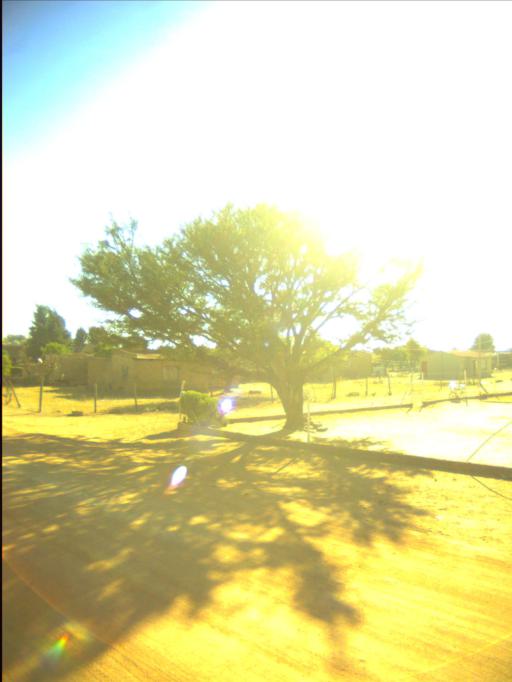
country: ZA
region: Mpumalanga
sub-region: Nkangala District Municipality
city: Siyabuswa
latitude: -25.1499
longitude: 28.9709
